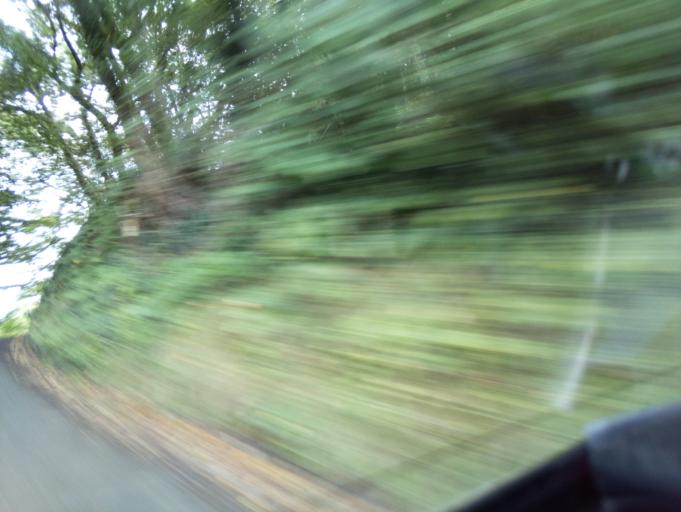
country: GB
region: Wales
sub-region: Cardiff
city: Pentyrch
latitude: 51.5587
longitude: -3.2760
